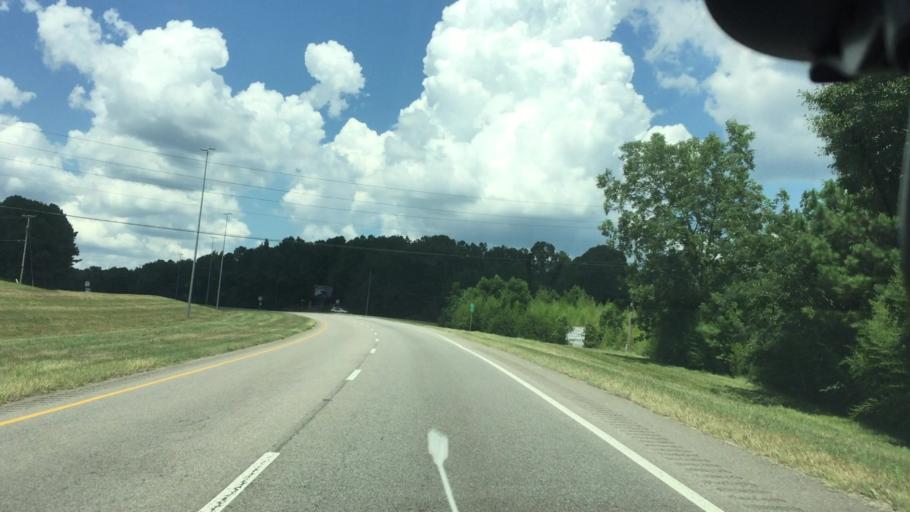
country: US
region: Alabama
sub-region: Pike County
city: Troy
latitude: 31.8306
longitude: -85.9915
